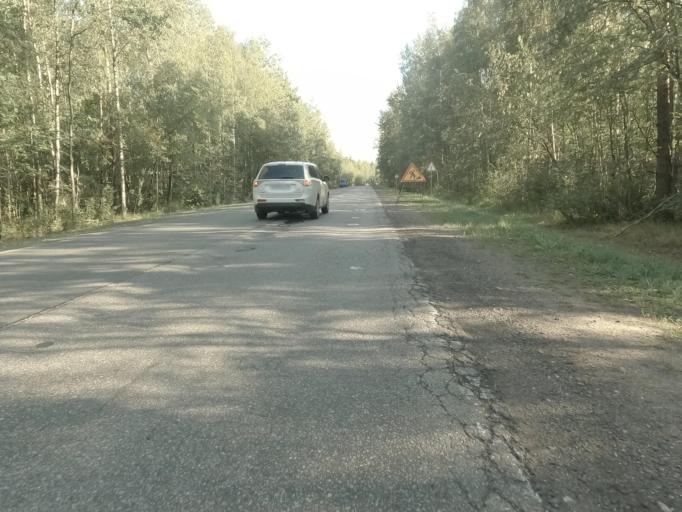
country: RU
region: Leningrad
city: Kirovsk
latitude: 59.9346
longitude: 30.9828
